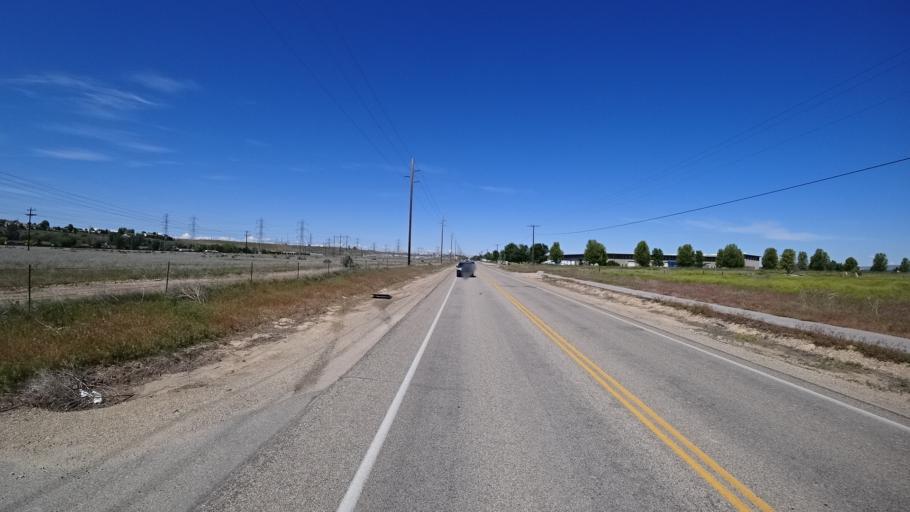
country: US
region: Idaho
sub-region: Ada County
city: Boise
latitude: 43.5599
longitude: -116.1452
